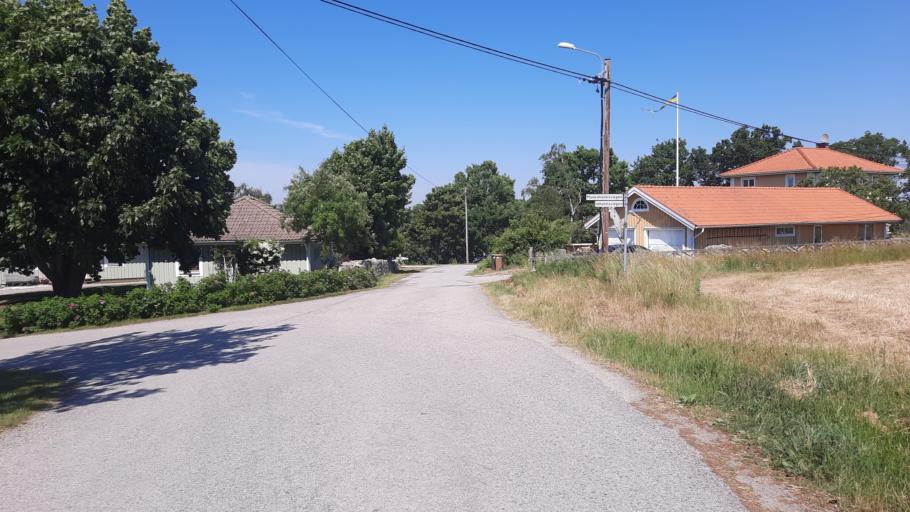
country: SE
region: Blekinge
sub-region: Karlskrona Kommun
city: Jaemjoe
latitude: 56.1527
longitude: 15.7589
